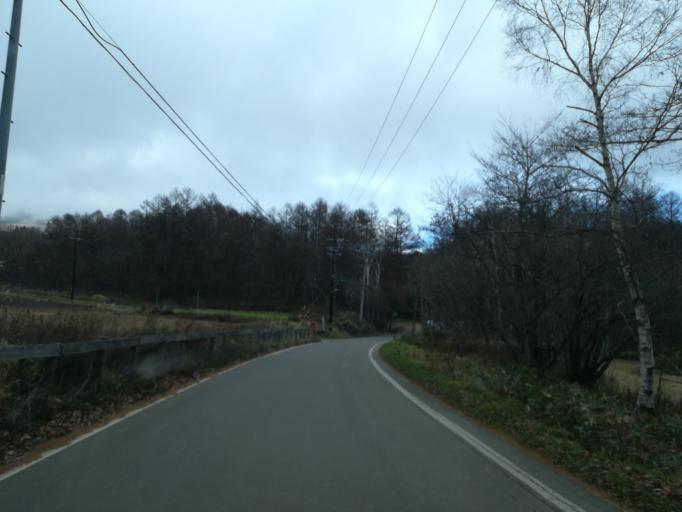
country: JP
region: Nagano
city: Suzaka
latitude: 36.5276
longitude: 138.3397
